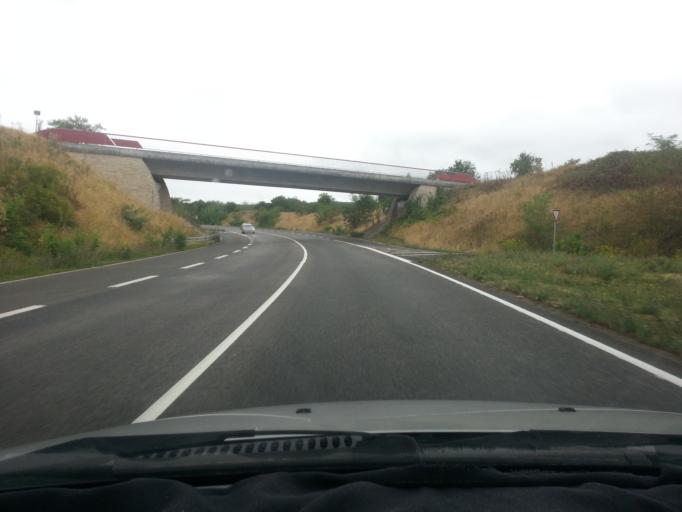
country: DE
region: Rheinland-Pfalz
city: Bad Duerkheim
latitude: 49.4606
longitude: 8.1822
